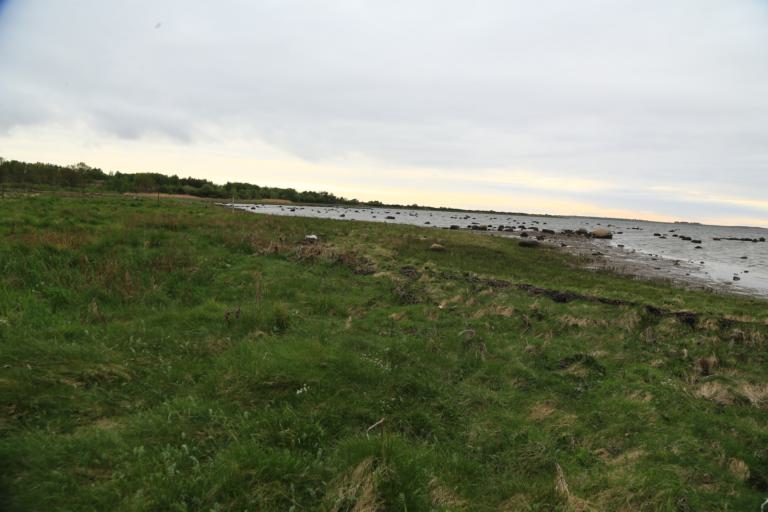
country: SE
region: Halland
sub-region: Varbergs Kommun
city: Varberg
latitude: 57.1536
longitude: 12.2244
